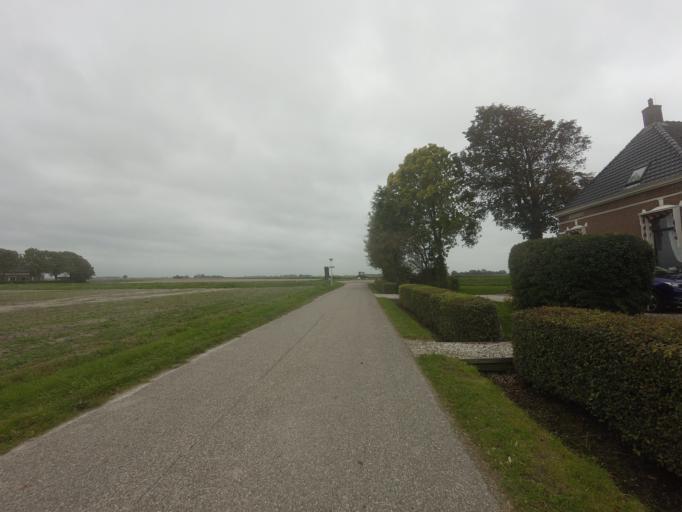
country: NL
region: Friesland
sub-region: Gemeente Ferwerderadiel
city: Ferwert
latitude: 53.3351
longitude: 5.8484
